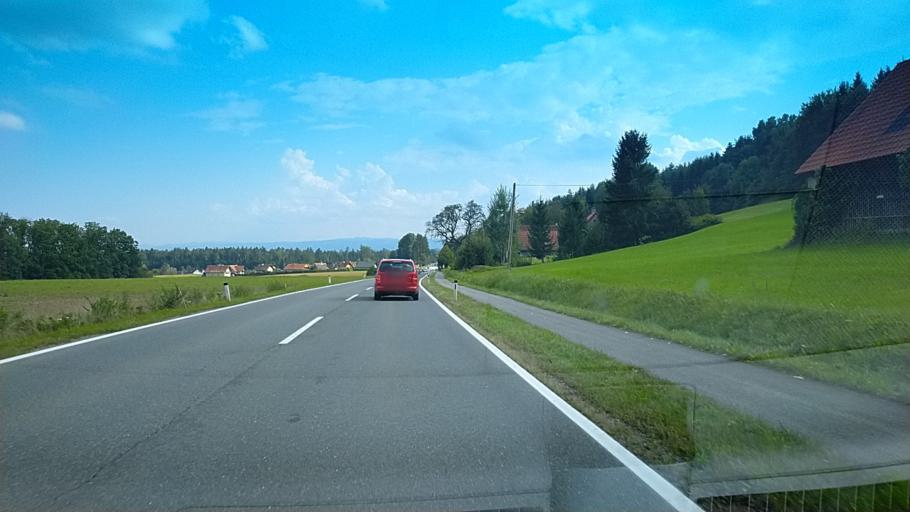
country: AT
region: Styria
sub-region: Politischer Bezirk Deutschlandsberg
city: Hollenegg
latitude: 46.7860
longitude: 15.2304
